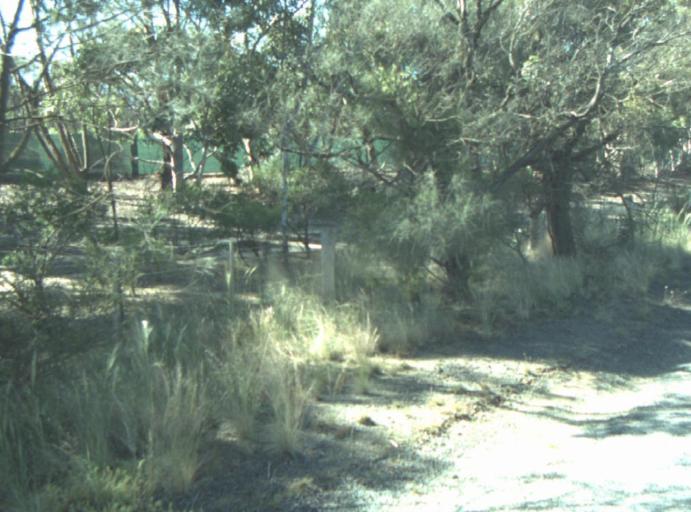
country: AU
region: Victoria
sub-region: Greater Geelong
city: Lara
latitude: -37.9083
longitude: 144.3989
